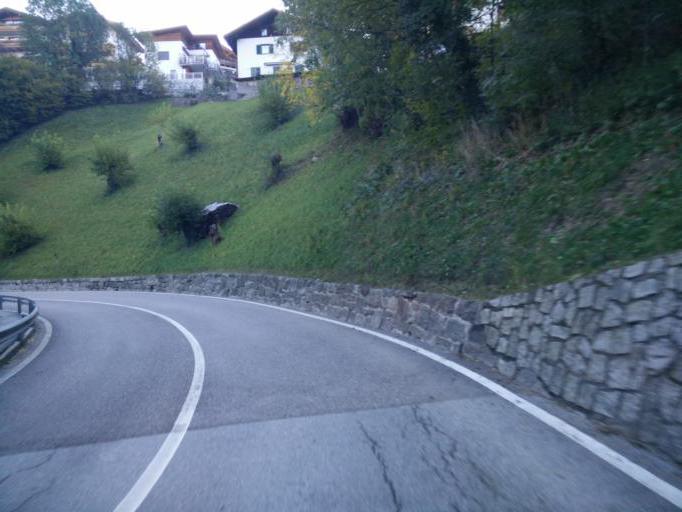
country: IT
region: Trentino-Alto Adige
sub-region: Bolzano
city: San Leonardo in Passiria
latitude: 46.8136
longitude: 11.2432
